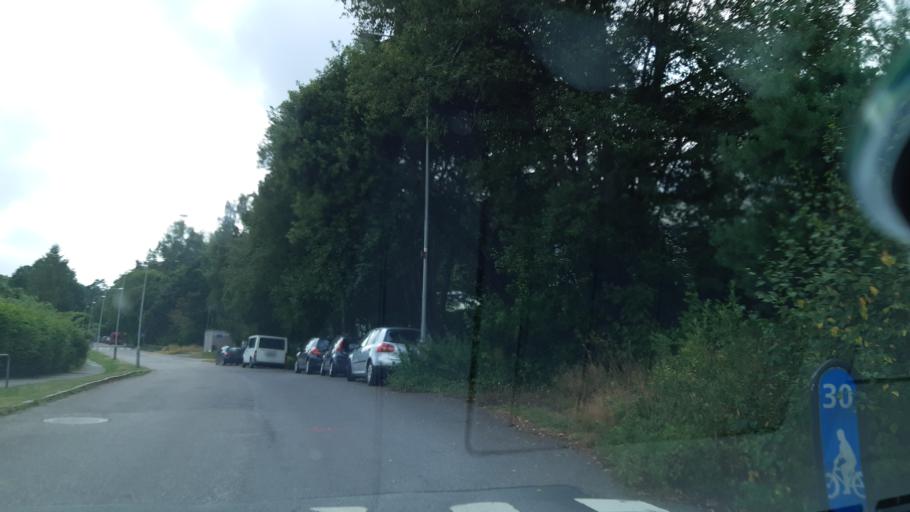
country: SE
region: Vaestra Goetaland
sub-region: Partille Kommun
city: Partille
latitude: 57.7162
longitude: 12.0604
